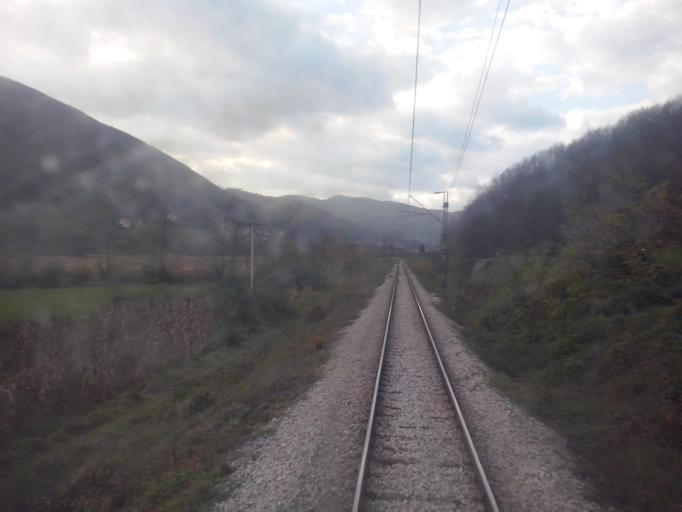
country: RS
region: Central Serbia
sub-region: Zlatiborski Okrug
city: Kosjeric
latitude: 43.9839
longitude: 19.9366
